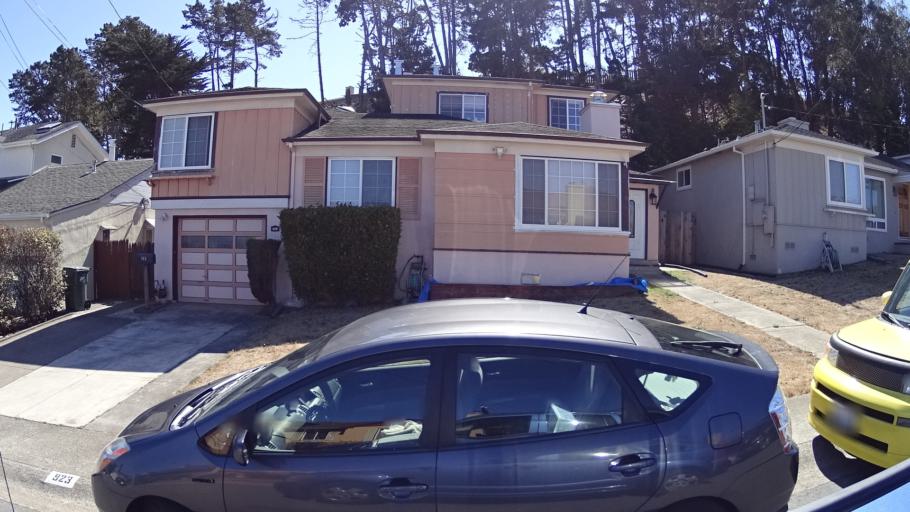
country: US
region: California
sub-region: San Mateo County
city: Broadmoor
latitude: 37.6948
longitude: -122.4872
